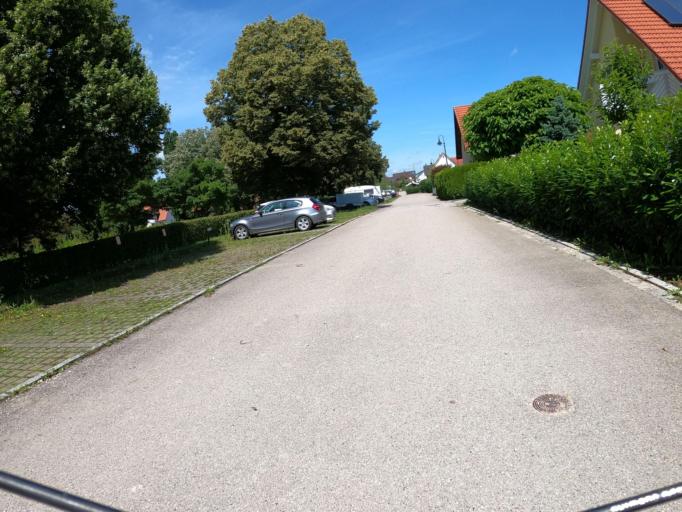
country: DE
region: Bavaria
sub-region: Swabia
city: Leipheim
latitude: 48.4440
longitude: 10.2174
